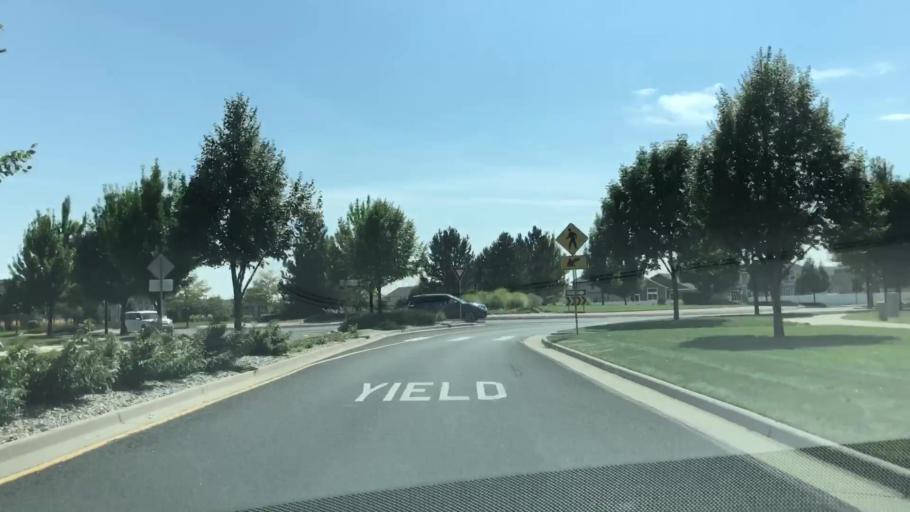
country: US
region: Colorado
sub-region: Larimer County
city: Loveland
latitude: 40.4052
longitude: -105.0353
